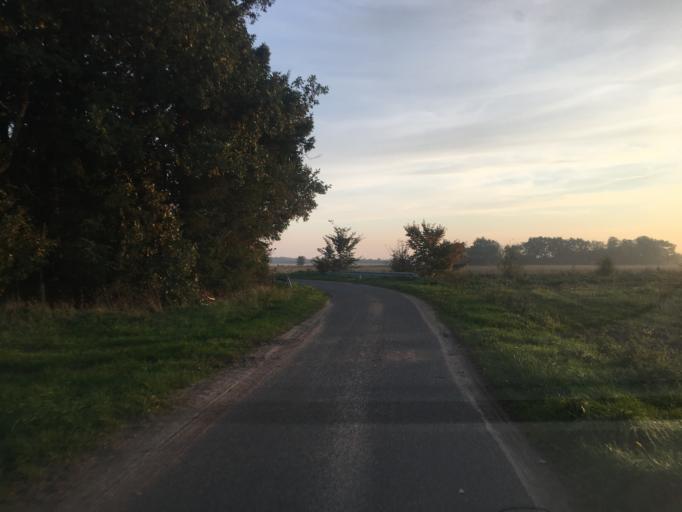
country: DK
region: South Denmark
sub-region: Tonder Kommune
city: Toftlund
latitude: 55.0337
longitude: 9.1170
